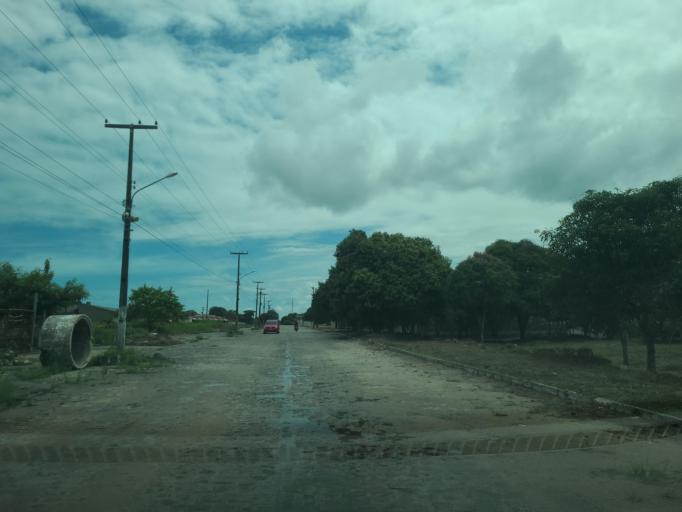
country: BR
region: Alagoas
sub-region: Satuba
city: Satuba
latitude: -9.5537
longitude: -35.7711
